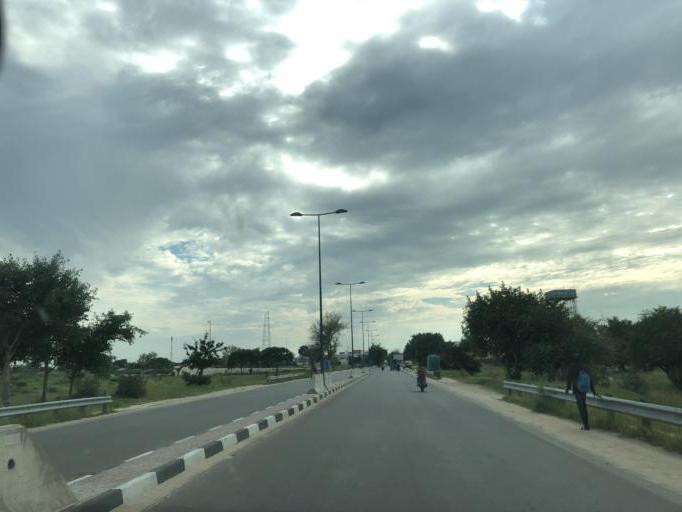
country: AO
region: Cunene
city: Ondjiva
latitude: -17.0694
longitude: 15.7181
